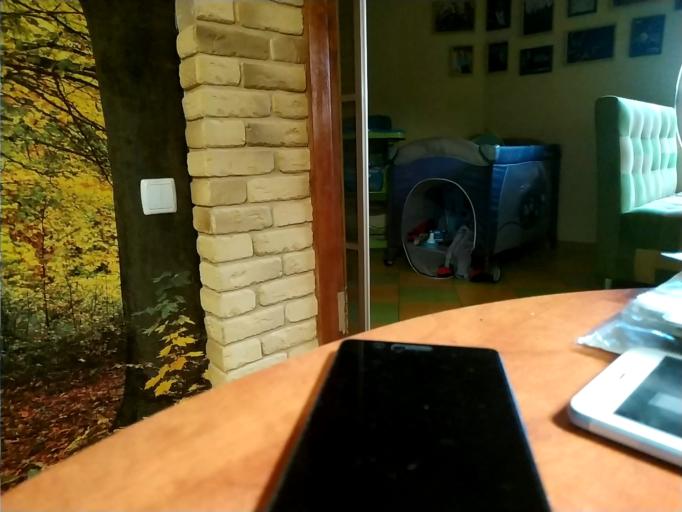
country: RU
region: Orjol
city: Znamenskoye
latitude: 53.5689
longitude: 35.4812
